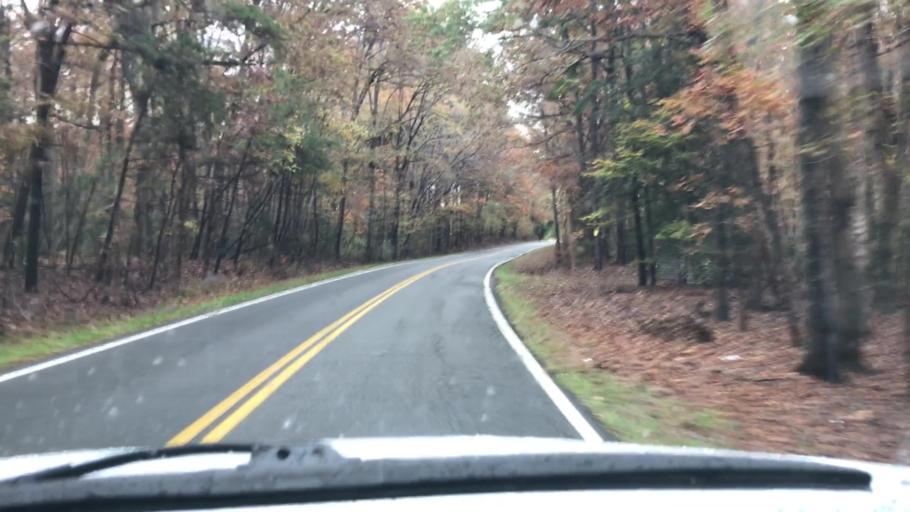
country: US
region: Virginia
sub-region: Henrico County
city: Short Pump
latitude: 37.6167
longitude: -77.6961
